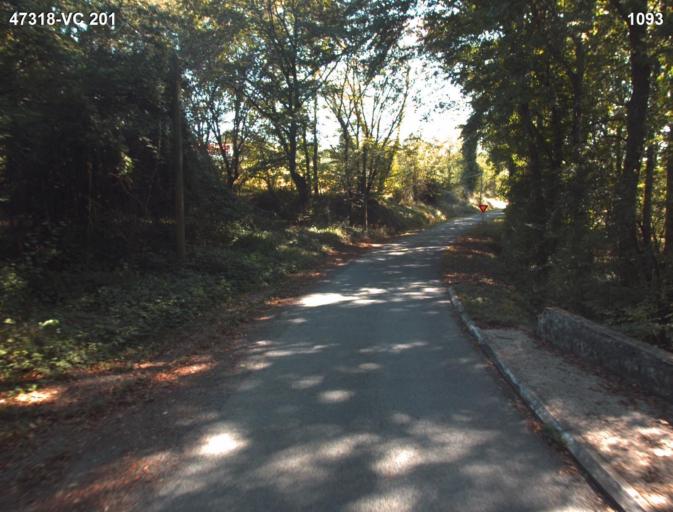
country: FR
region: Aquitaine
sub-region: Departement du Lot-et-Garonne
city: Vianne
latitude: 44.2068
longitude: 0.3159
